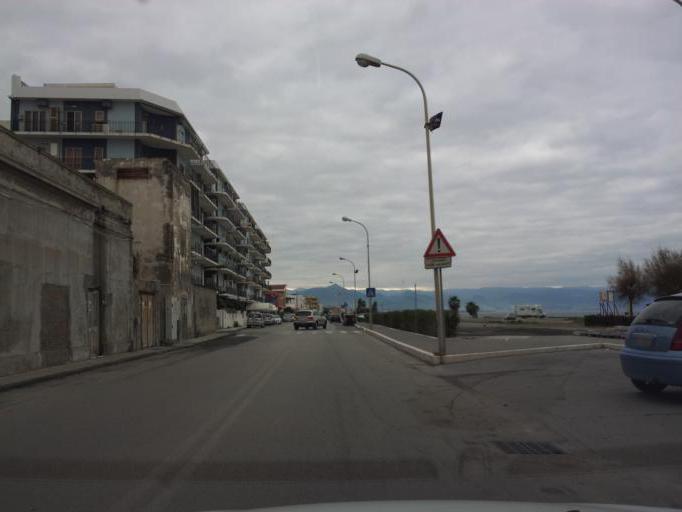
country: IT
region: Sicily
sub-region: Messina
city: Milazzo
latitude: 38.2200
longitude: 15.2336
